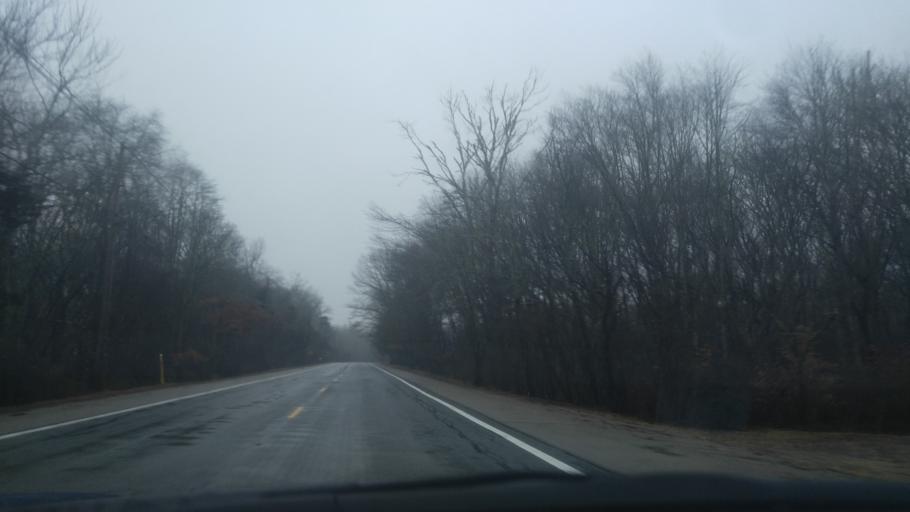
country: US
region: Rhode Island
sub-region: Washington County
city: Kingston
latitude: 41.4824
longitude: -71.5893
